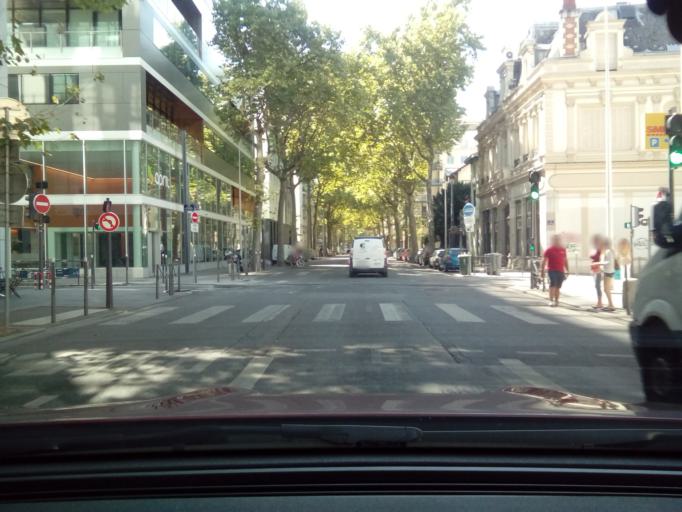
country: FR
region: Rhone-Alpes
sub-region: Departement du Rhone
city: Lyon
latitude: 45.7536
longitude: 4.8582
